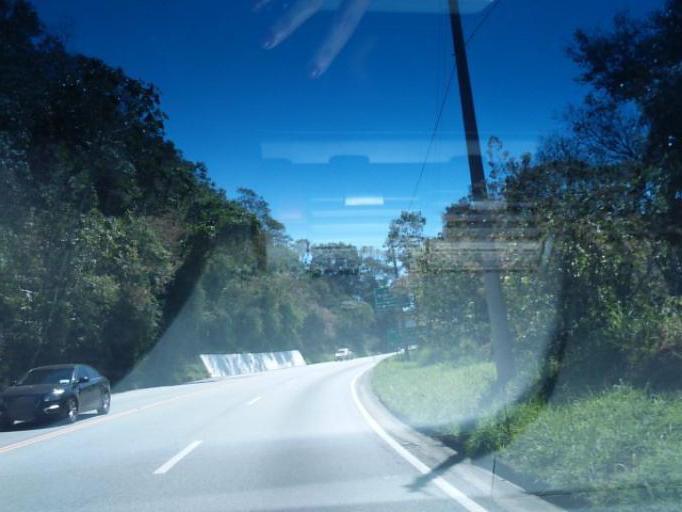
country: BR
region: Sao Paulo
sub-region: Campos Do Jordao
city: Campos do Jordao
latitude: -22.8339
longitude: -45.6240
